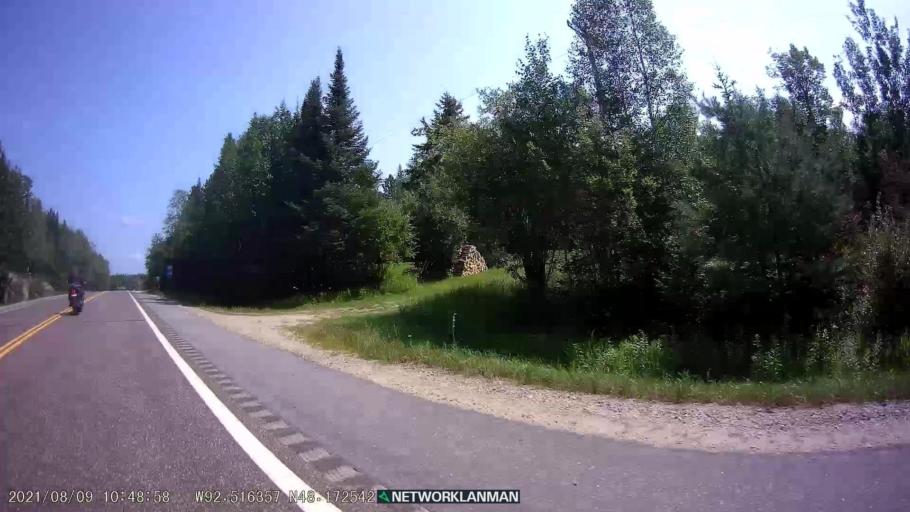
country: US
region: Minnesota
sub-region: Saint Louis County
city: Parkville
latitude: 48.1725
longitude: -92.5163
